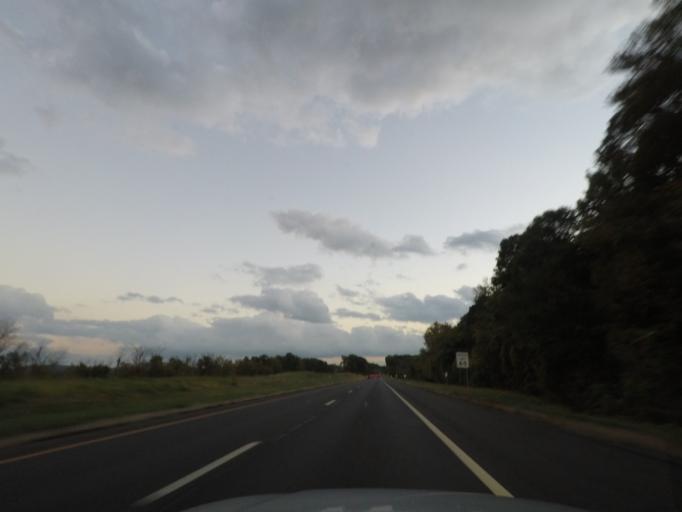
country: US
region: New York
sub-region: Ulster County
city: New Paltz
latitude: 41.7657
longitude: -74.0548
